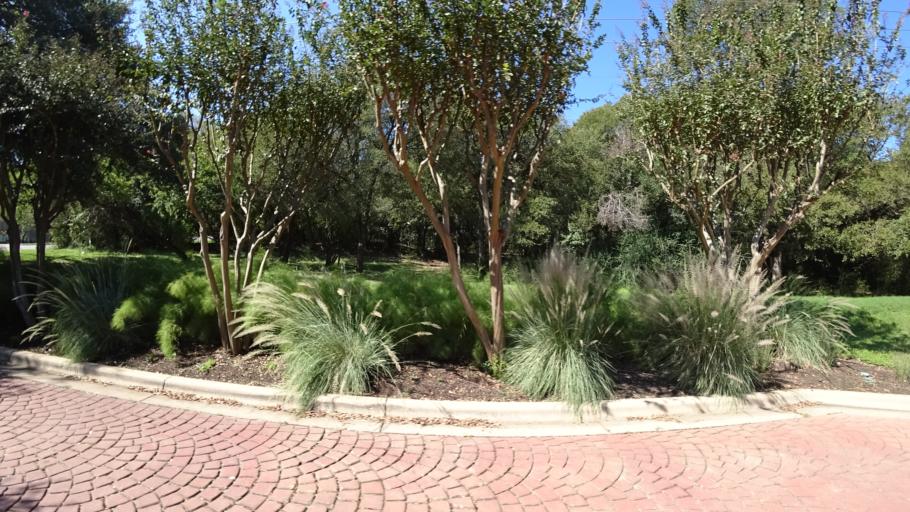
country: US
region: Texas
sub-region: Travis County
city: Rollingwood
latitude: 30.2738
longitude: -97.7974
